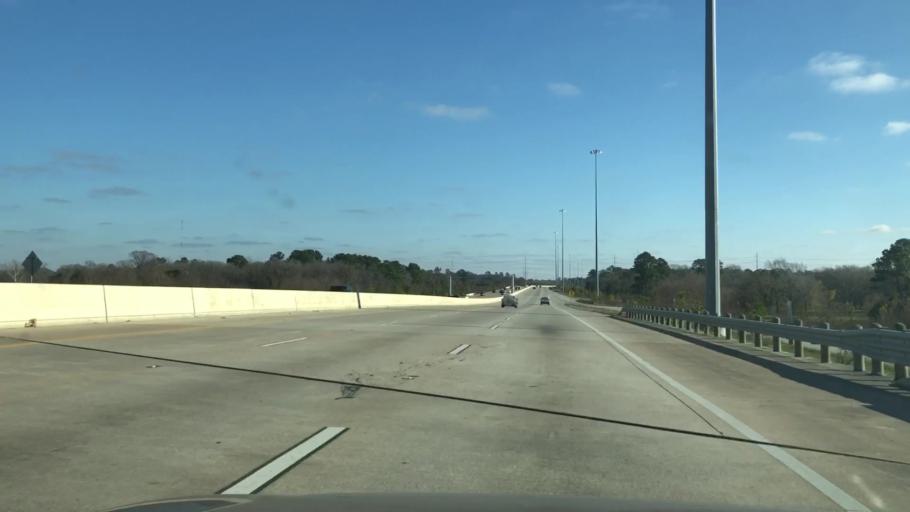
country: US
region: Texas
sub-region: Harris County
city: Jacinto City
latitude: 29.7851
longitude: -95.2456
